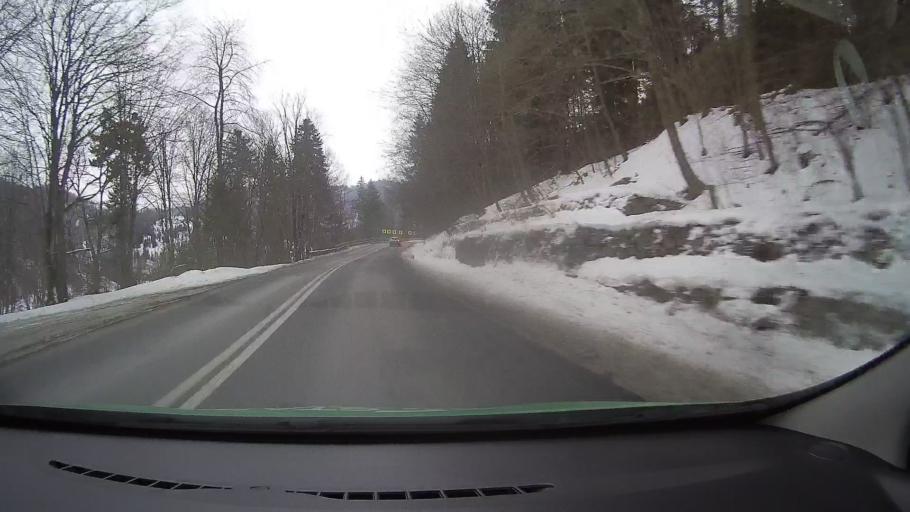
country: RO
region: Brasov
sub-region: Oras Predeal
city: Predeal
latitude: 45.5222
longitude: 25.5071
